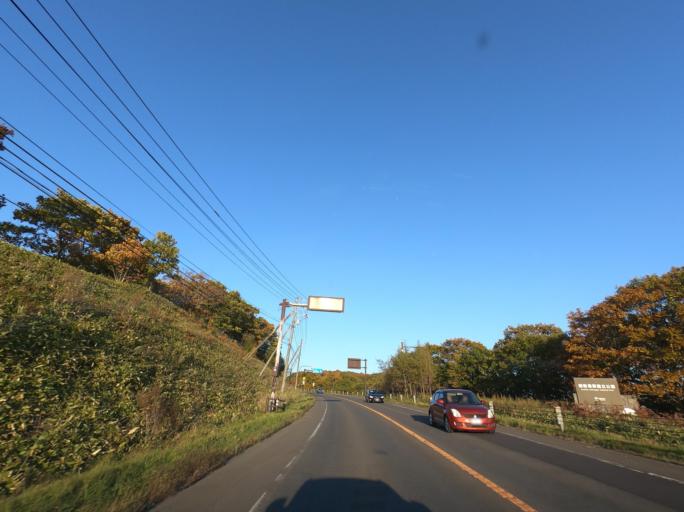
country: JP
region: Hokkaido
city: Kushiro
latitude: 43.0687
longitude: 144.3156
